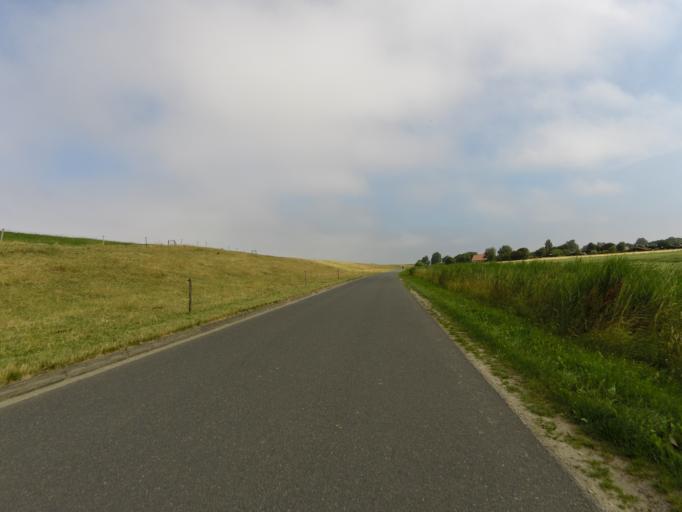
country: DE
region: Lower Saxony
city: Nordholz
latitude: 53.7810
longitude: 8.5498
